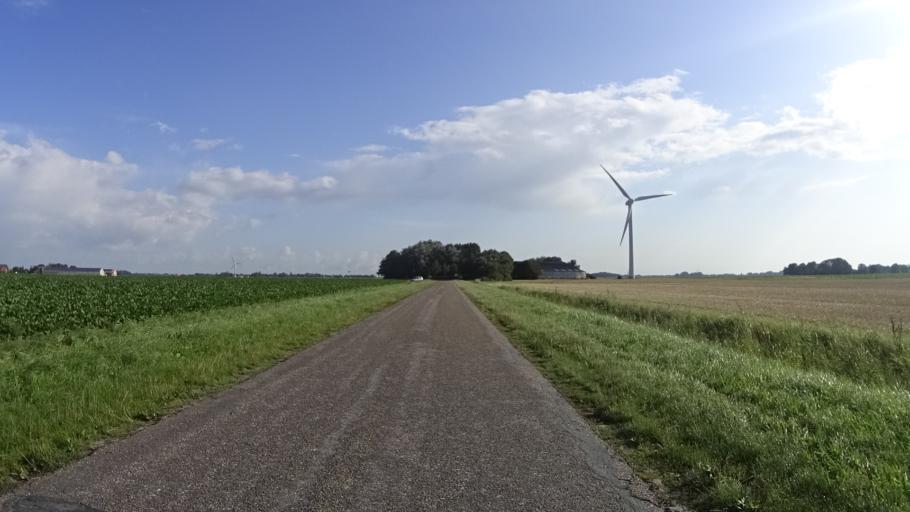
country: NL
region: Friesland
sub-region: Gemeente Harlingen
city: Harlingen
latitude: 53.1208
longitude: 5.4304
